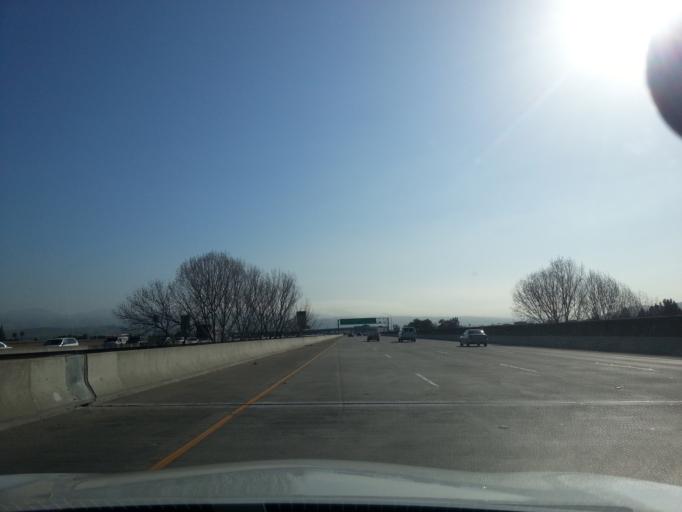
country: US
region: California
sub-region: Santa Clara County
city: Seven Trees
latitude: 37.2558
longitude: -121.8705
